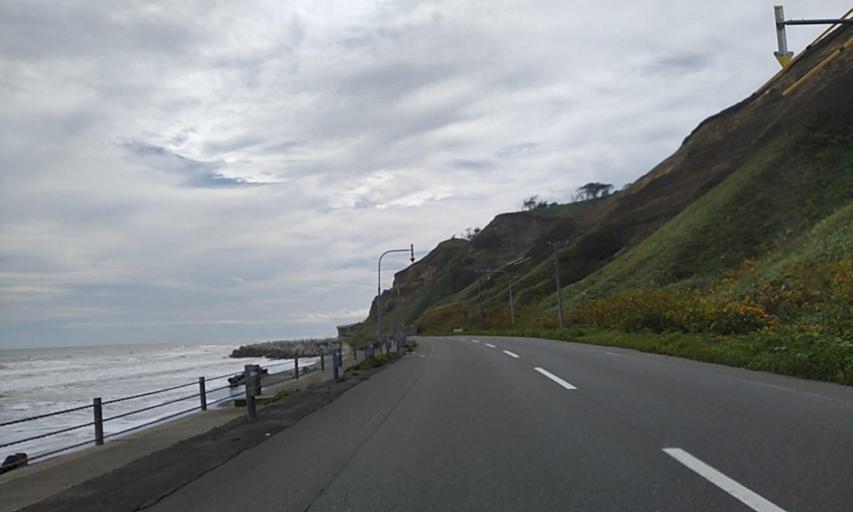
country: JP
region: Hokkaido
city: Obihiro
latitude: 42.7736
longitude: 143.7747
